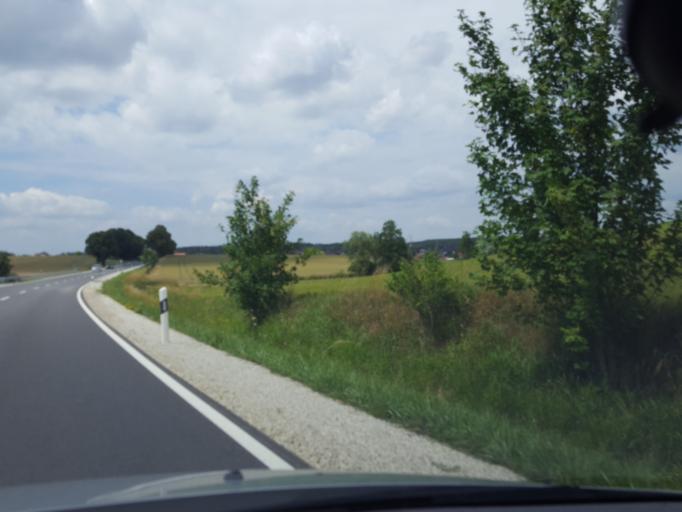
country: DE
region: Bavaria
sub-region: Lower Bavaria
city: Furth
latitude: 48.4182
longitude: 12.4152
